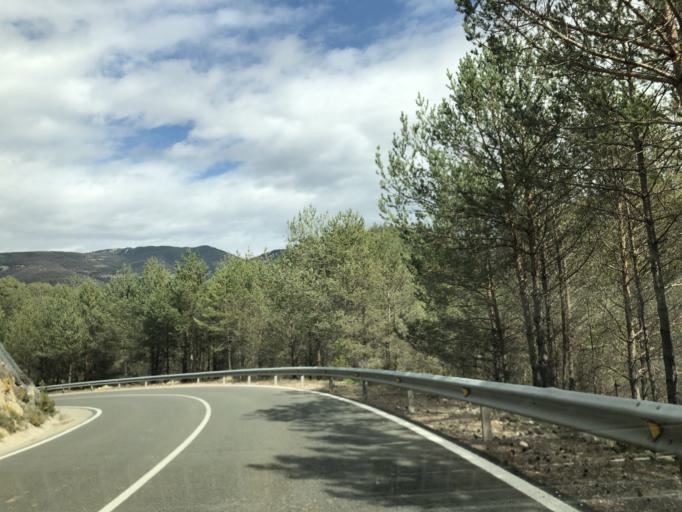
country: ES
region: Catalonia
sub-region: Provincia de Barcelona
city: Capolat
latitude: 42.1180
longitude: 1.6931
